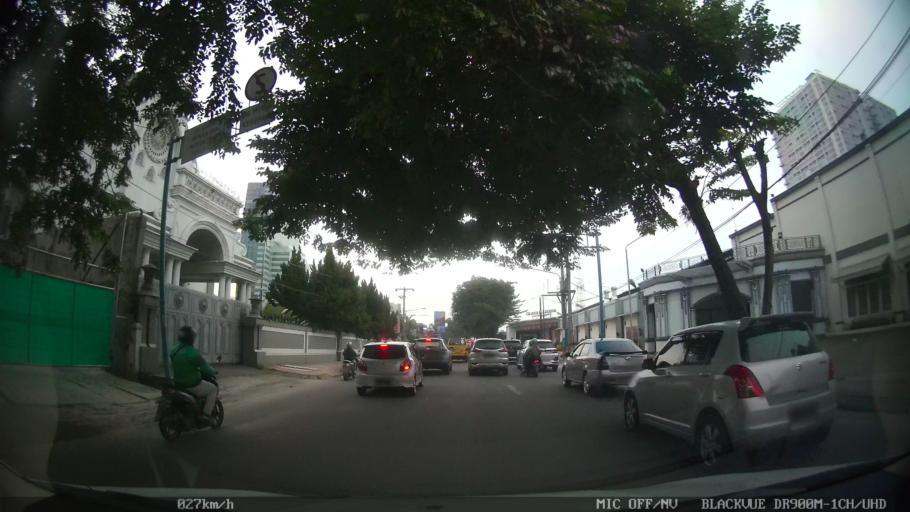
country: ID
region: North Sumatra
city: Medan
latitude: 3.5945
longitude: 98.6778
